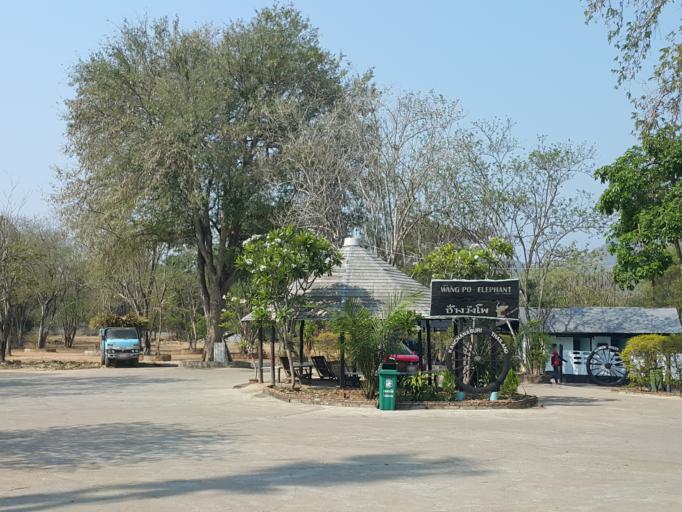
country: TH
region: Kanchanaburi
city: Sai Yok
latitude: 14.1141
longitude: 99.1359
